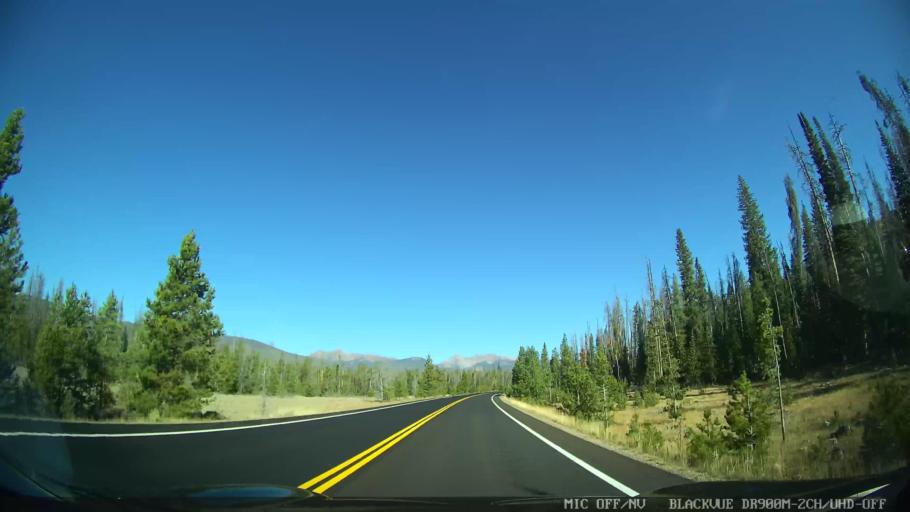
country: US
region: Colorado
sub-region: Grand County
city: Granby
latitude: 40.2851
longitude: -105.8413
